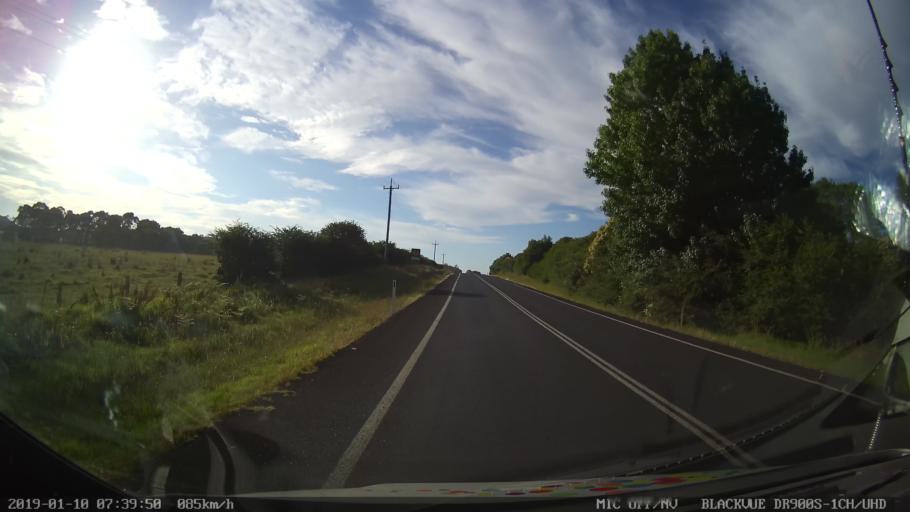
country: AU
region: New South Wales
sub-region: Bellingen
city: Dorrigo
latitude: -30.3615
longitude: 152.7198
